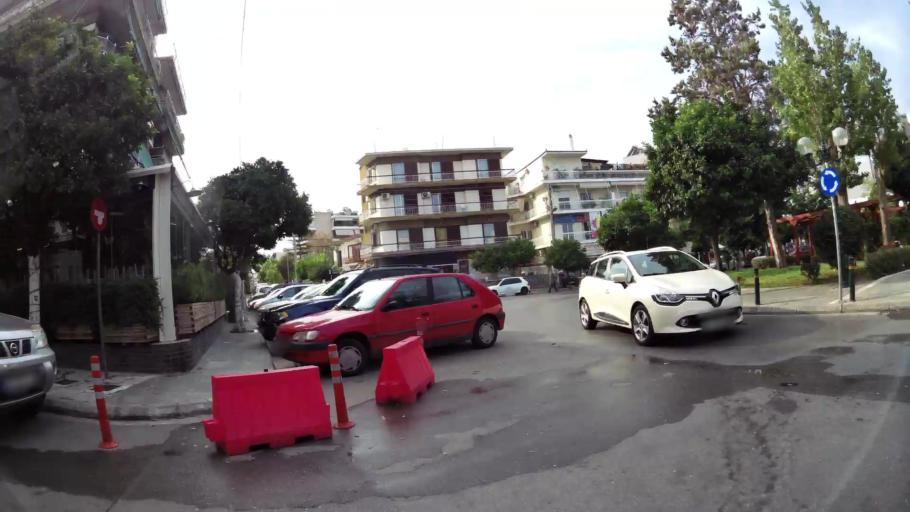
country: GR
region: Attica
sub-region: Nomarchia Athinas
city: Palaio Faliro
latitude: 37.9313
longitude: 23.7036
